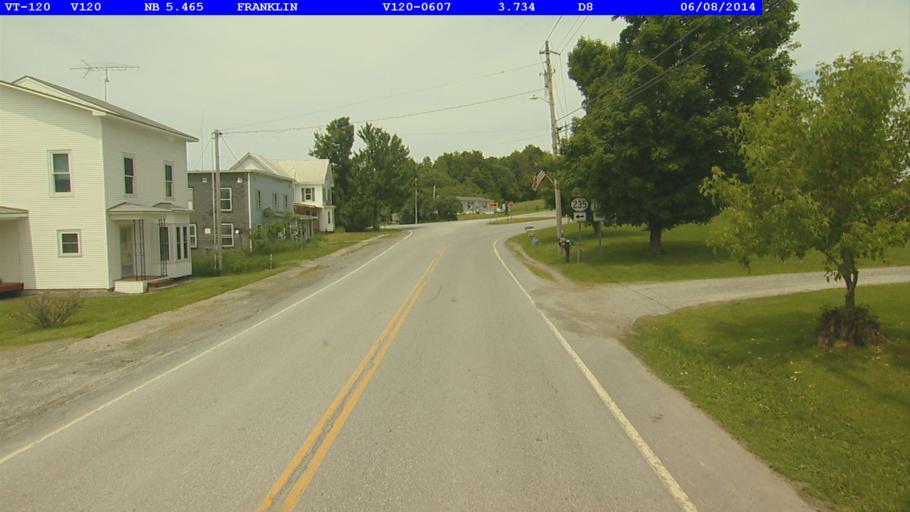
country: US
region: Vermont
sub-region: Franklin County
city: Enosburg Falls
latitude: 44.9855
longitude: -72.9176
